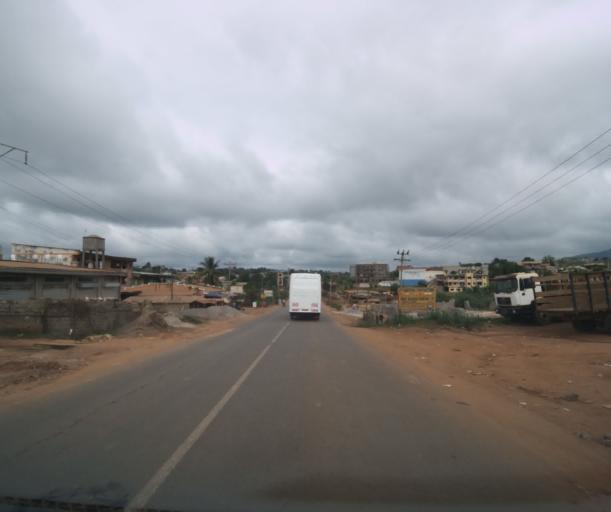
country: CM
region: Centre
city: Yaounde
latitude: 3.7948
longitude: 11.4926
